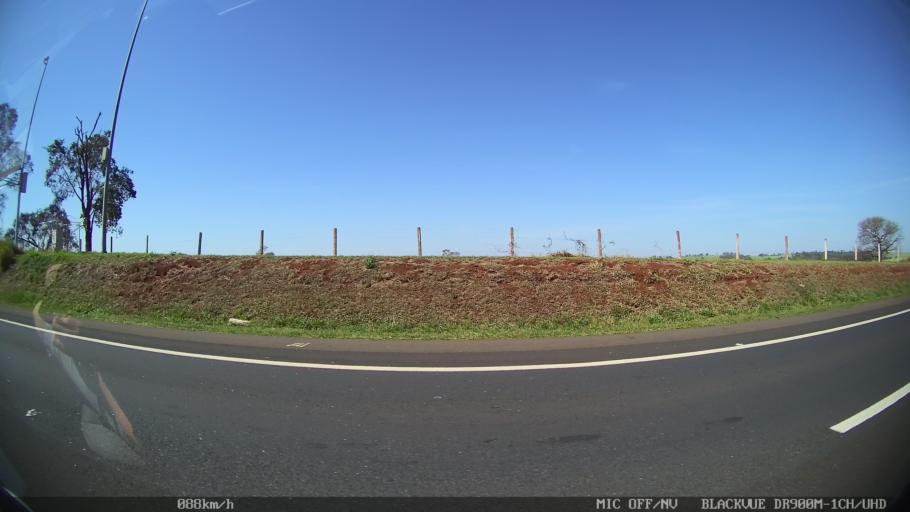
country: BR
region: Sao Paulo
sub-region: Batatais
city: Batatais
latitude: -20.7941
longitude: -47.5631
